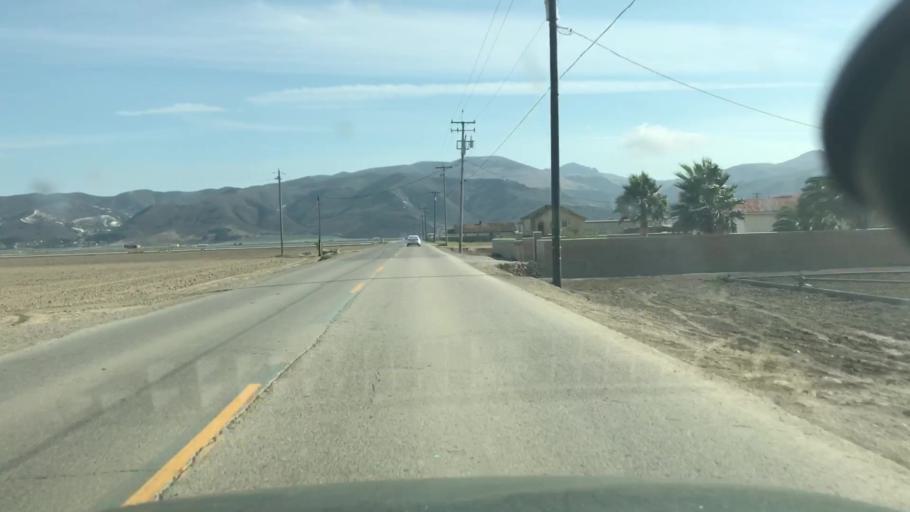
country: US
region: California
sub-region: Santa Barbara County
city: Lompoc
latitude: 34.6550
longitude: -120.4930
